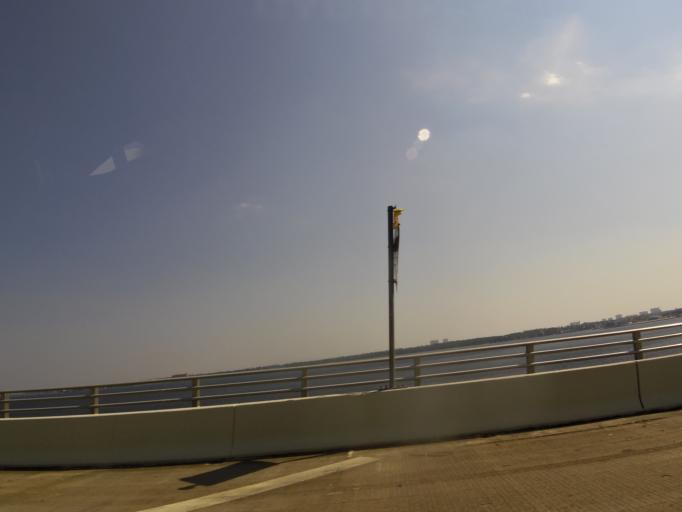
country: US
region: Florida
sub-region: Bay County
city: Upper Grand Lagoon
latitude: 30.1875
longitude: -85.7436
